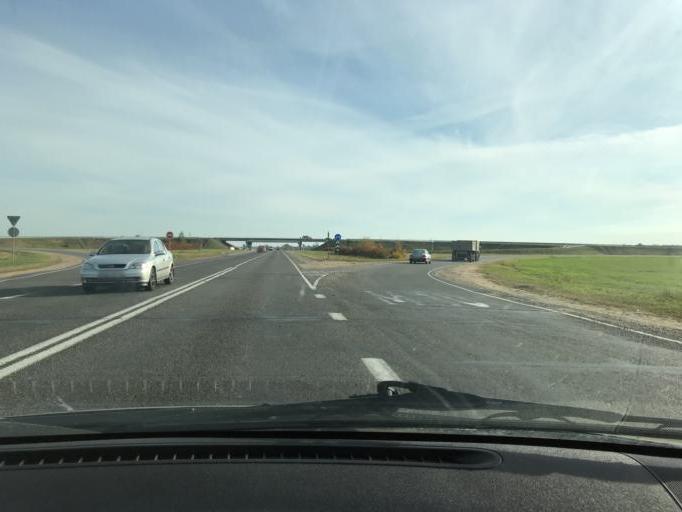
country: BY
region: Brest
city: Asnyezhytsy
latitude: 52.1876
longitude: 26.0771
